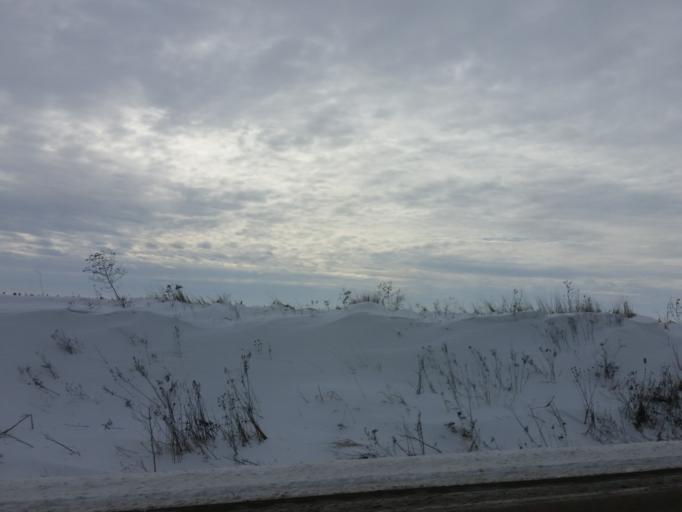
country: US
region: Iowa
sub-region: Dubuque County
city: Peosta
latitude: 42.3821
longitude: -90.7423
